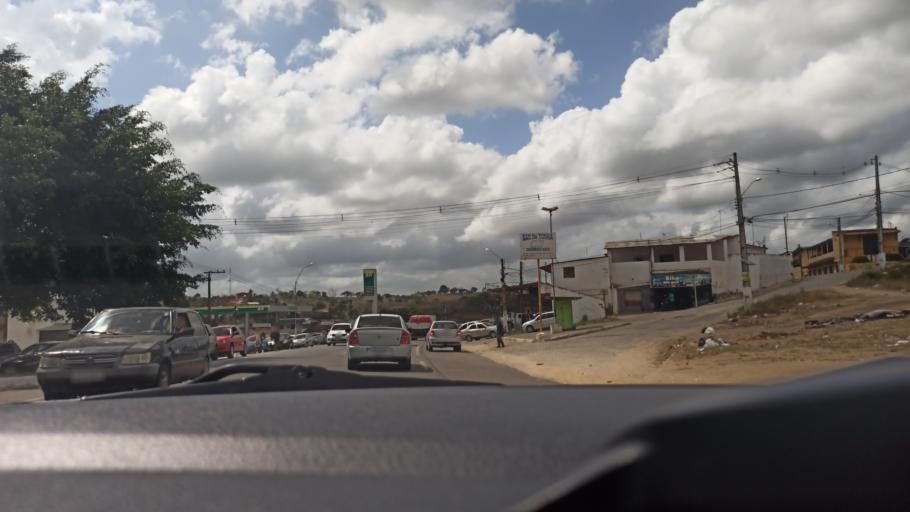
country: BR
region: Pernambuco
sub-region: Nazare Da Mata
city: Nazare da Mata
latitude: -7.7501
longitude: -35.2329
